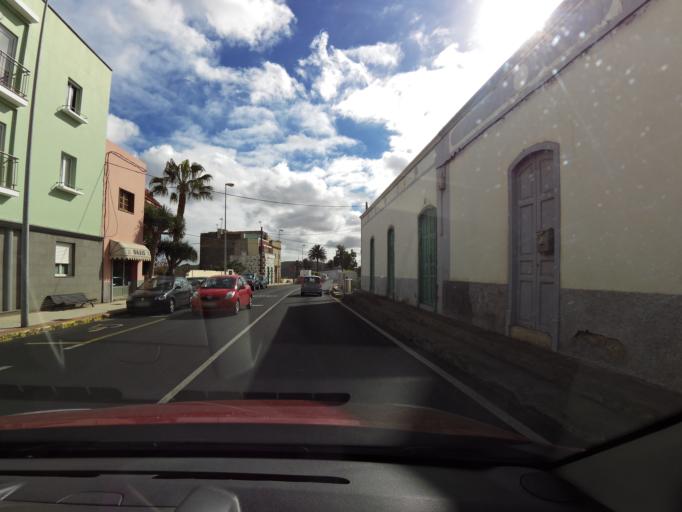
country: ES
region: Canary Islands
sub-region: Provincia de Las Palmas
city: Ingenio
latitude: 27.9178
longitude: -15.4387
